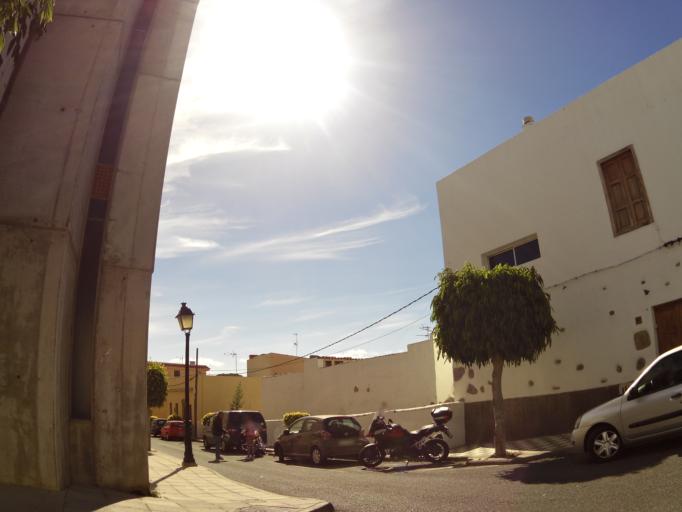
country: ES
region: Canary Islands
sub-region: Provincia de Las Palmas
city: Aguimes
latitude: 27.9059
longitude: -15.4469
